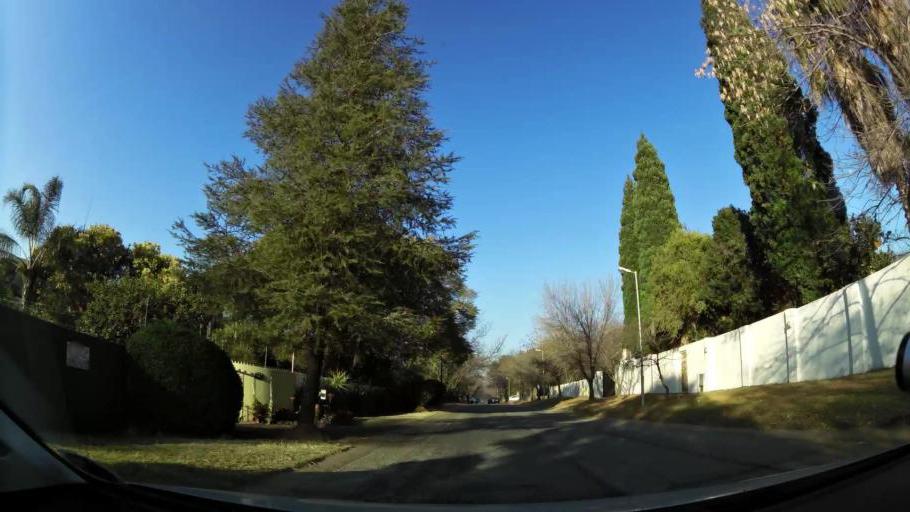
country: ZA
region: Gauteng
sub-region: City of Johannesburg Metropolitan Municipality
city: Midrand
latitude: -26.0462
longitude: 28.1050
